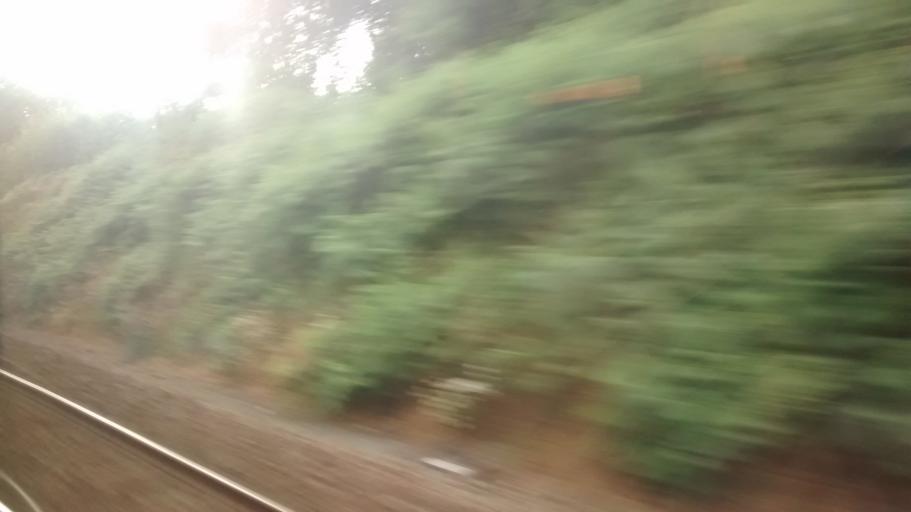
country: FR
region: Brittany
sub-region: Departement d'Ille-et-Vilaine
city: Poce-les-Bois
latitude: 48.1142
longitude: -1.2346
